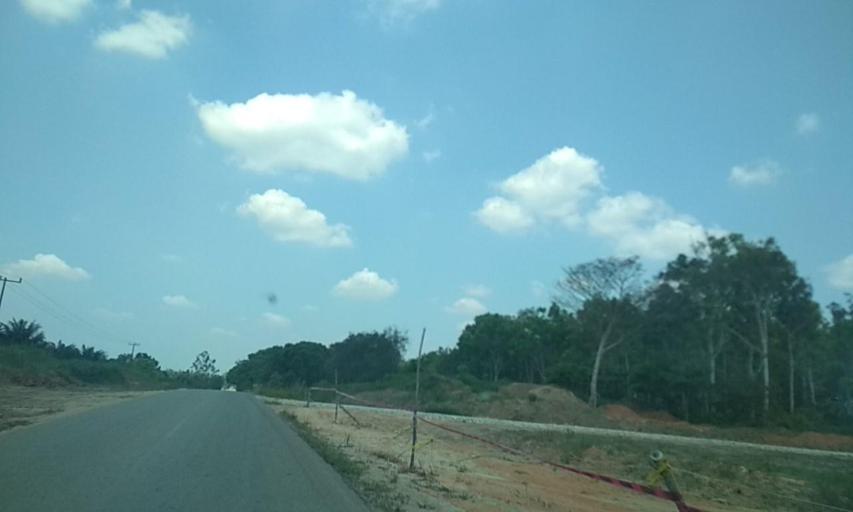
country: MX
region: Tabasco
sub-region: Huimanguillo
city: Paso de la Mina 2da. Seccion (Barrial)
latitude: 17.7611
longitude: -93.6558
